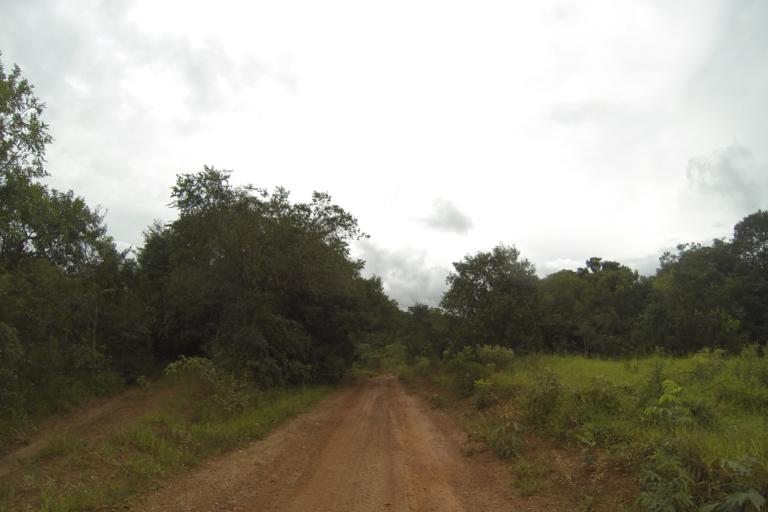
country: BR
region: Minas Gerais
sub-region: Ibia
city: Ibia
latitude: -19.7400
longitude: -46.5460
